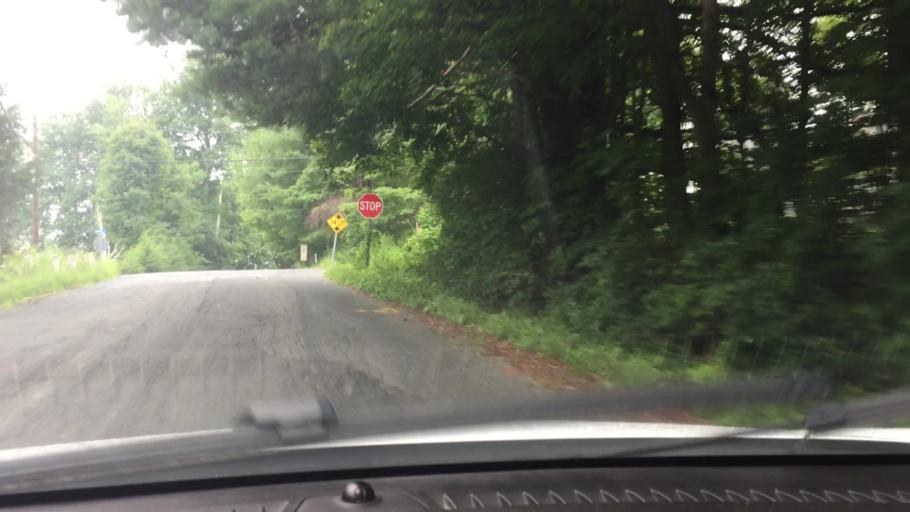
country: US
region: Massachusetts
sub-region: Berkshire County
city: Lee
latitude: 42.3034
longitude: -73.2810
